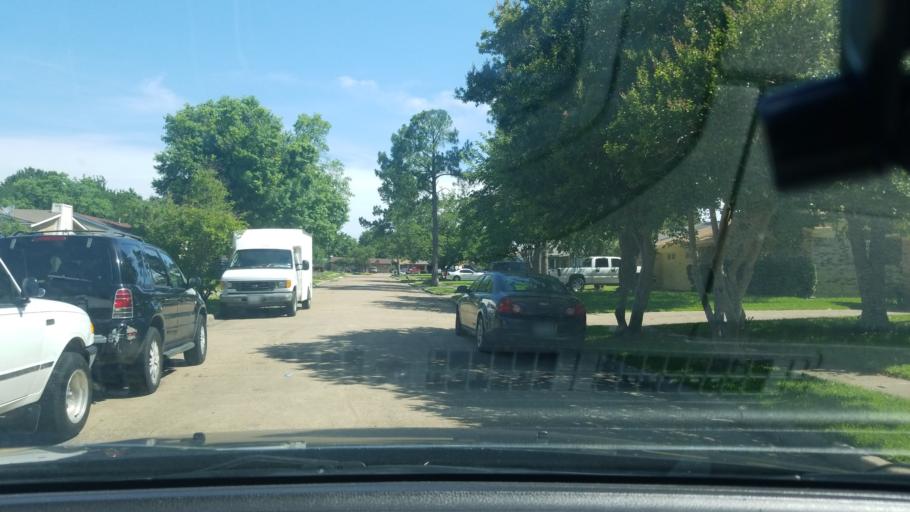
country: US
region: Texas
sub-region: Dallas County
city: Mesquite
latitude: 32.7712
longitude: -96.5951
